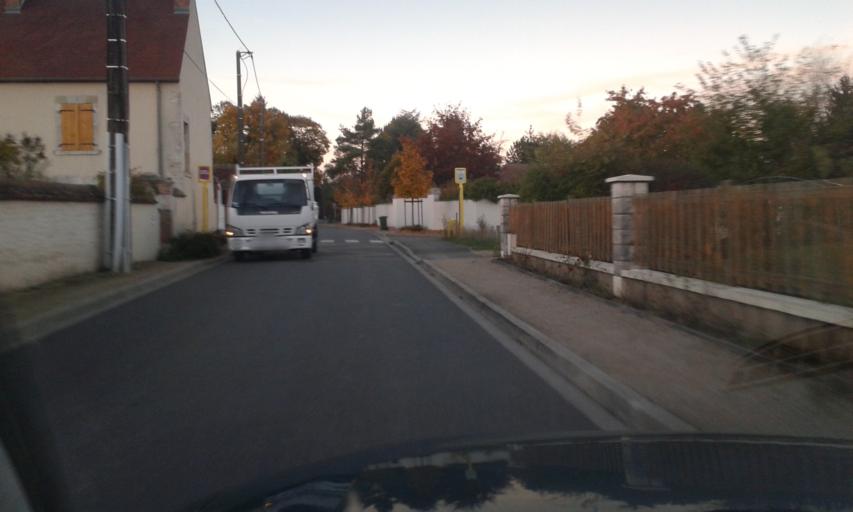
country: FR
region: Centre
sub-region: Departement du Loiret
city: Olivet
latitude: 47.8548
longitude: 1.8819
